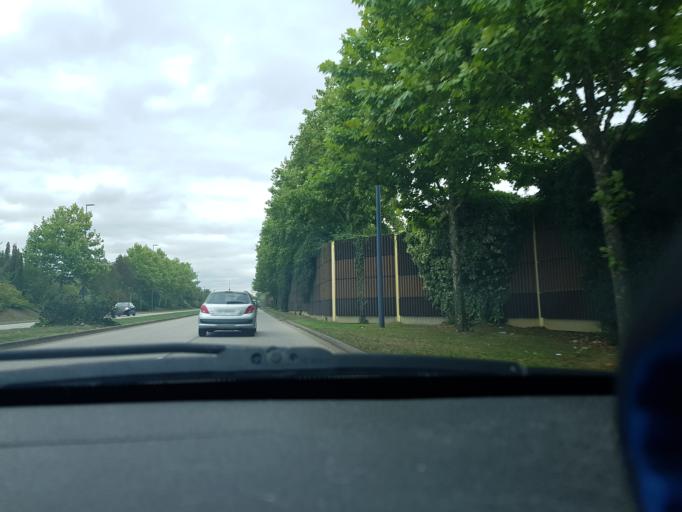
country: FR
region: Lorraine
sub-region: Departement de Meurthe-et-Moselle
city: Tomblaine
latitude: 48.6819
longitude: 6.2172
